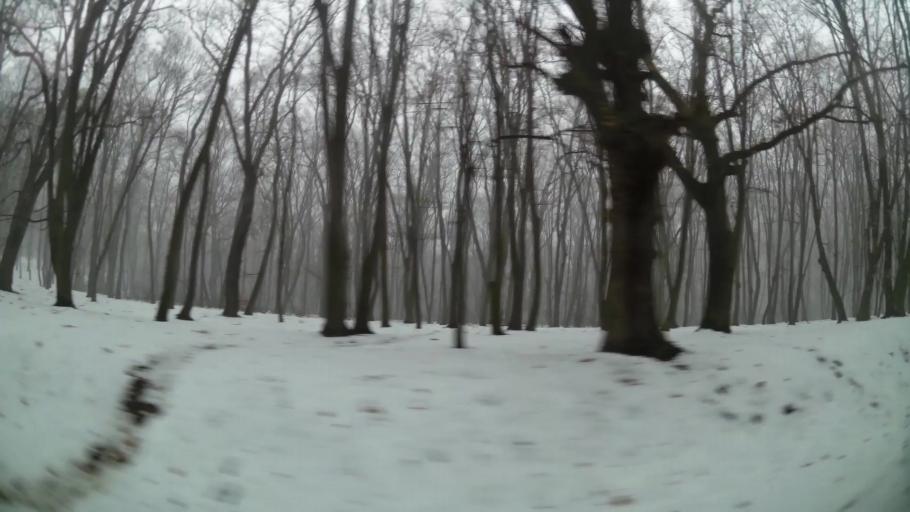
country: RS
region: Central Serbia
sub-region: Belgrade
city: Cukarica
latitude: 44.7732
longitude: 20.4256
